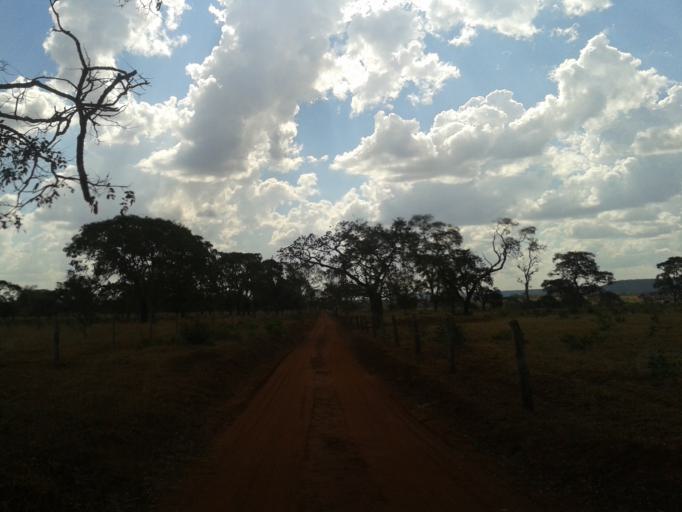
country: BR
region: Minas Gerais
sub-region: Santa Vitoria
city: Santa Vitoria
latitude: -19.1924
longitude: -49.9755
